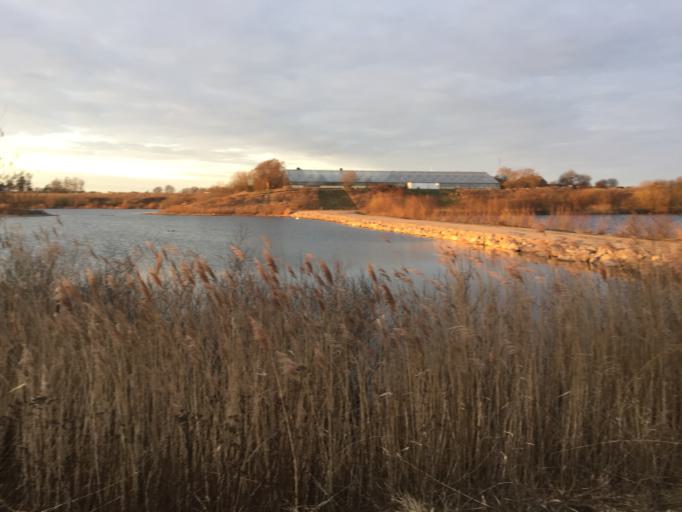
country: DK
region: South Denmark
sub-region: Kerteminde Kommune
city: Langeskov
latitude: 55.3285
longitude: 10.5326
